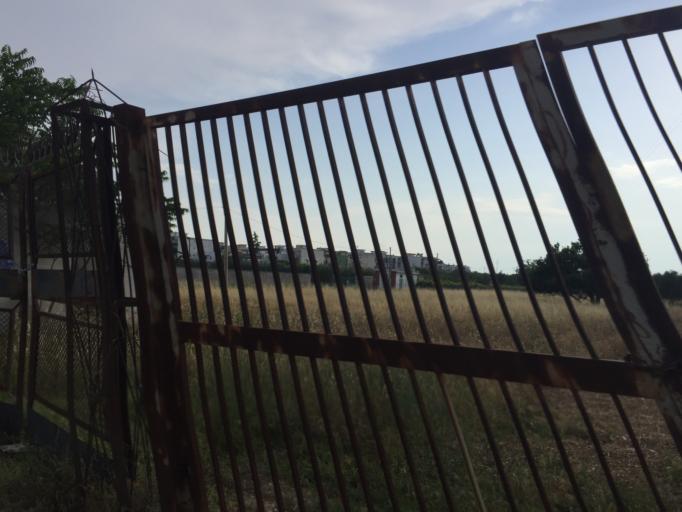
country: IT
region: Apulia
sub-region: Provincia di Bari
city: Capurso
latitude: 41.0539
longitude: 16.9214
